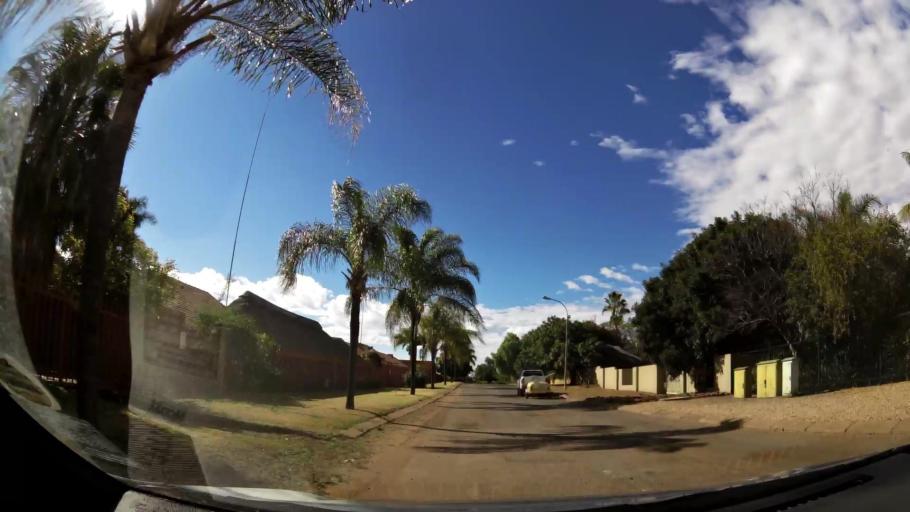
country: ZA
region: Limpopo
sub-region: Waterberg District Municipality
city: Warmbaths
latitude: -24.8708
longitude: 28.2878
